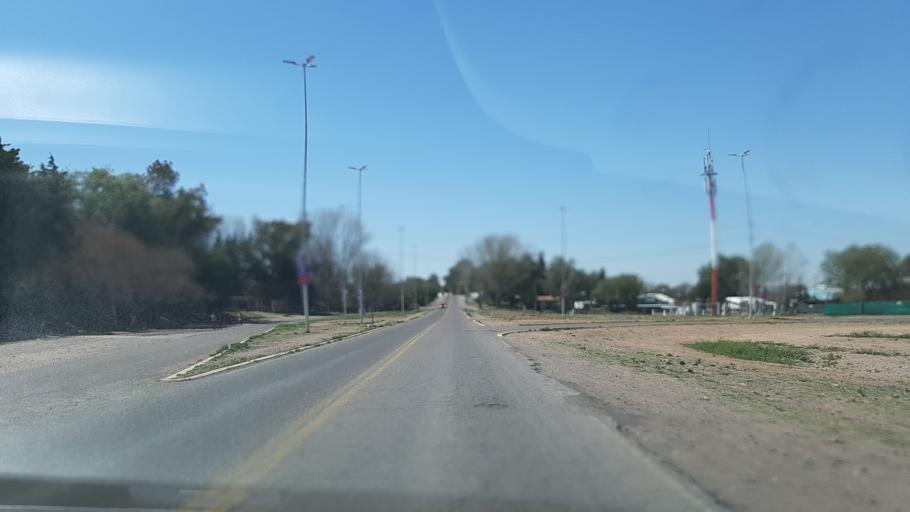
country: AR
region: Mendoza
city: Lujan de Cuyo
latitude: -33.0156
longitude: -68.9318
